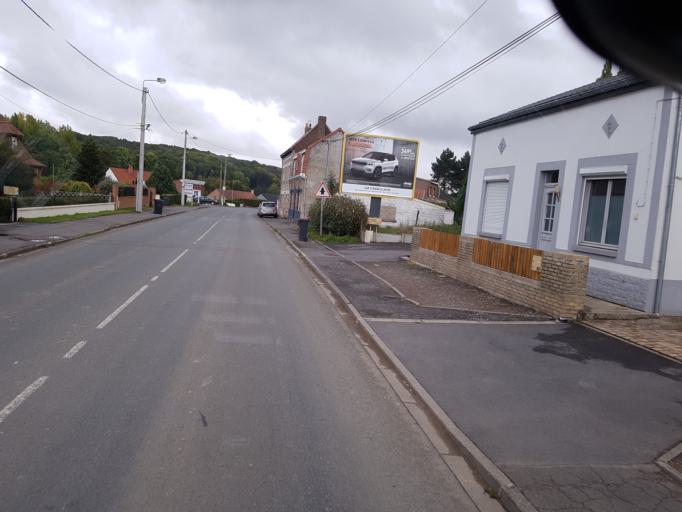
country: FR
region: Nord-Pas-de-Calais
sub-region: Departement du Pas-de-Calais
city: Angres
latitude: 50.4033
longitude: 2.7558
